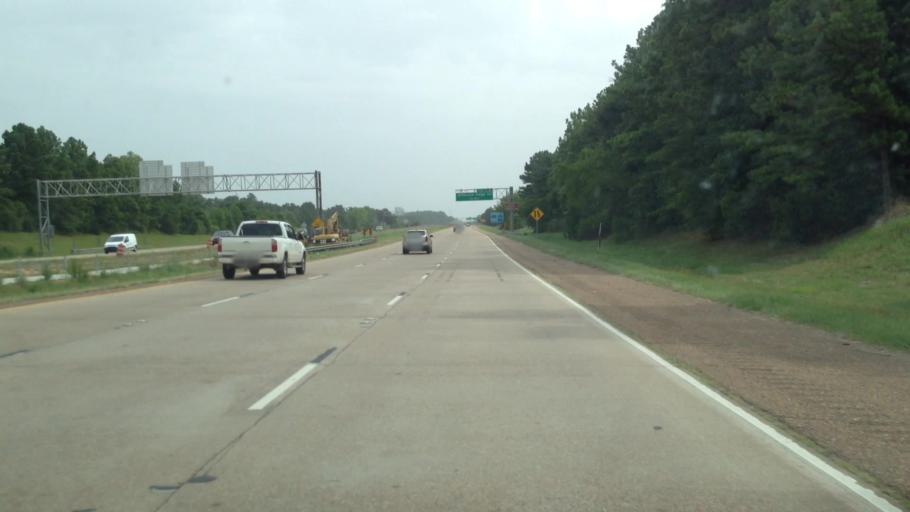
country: US
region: Louisiana
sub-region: Caddo Parish
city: Shreveport
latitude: 32.4632
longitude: -93.8444
